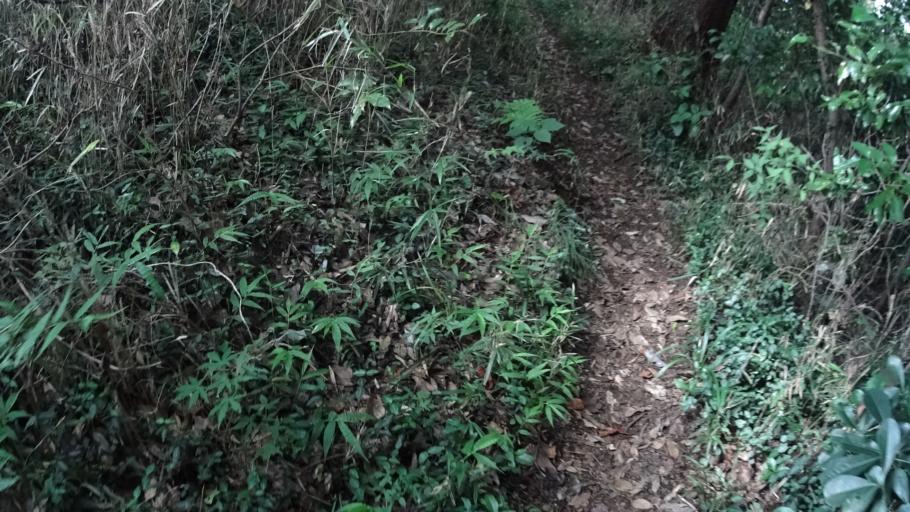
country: JP
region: Kanagawa
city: Zushi
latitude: 35.3159
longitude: 139.6040
